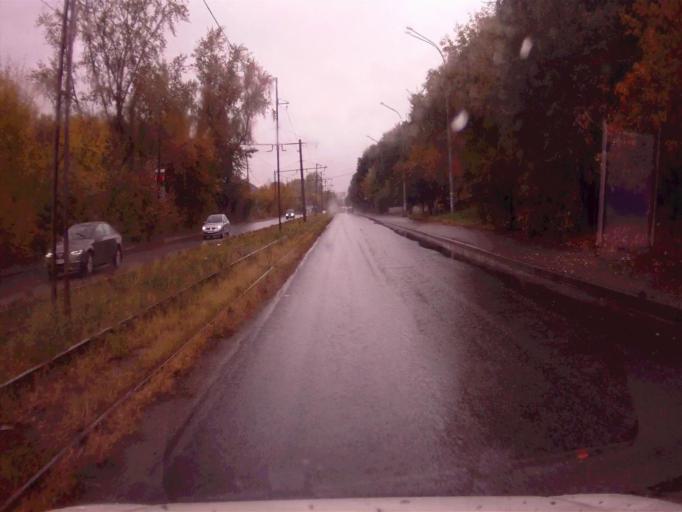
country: RU
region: Chelyabinsk
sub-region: Gorod Chelyabinsk
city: Chelyabinsk
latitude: 55.1751
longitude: 61.4151
